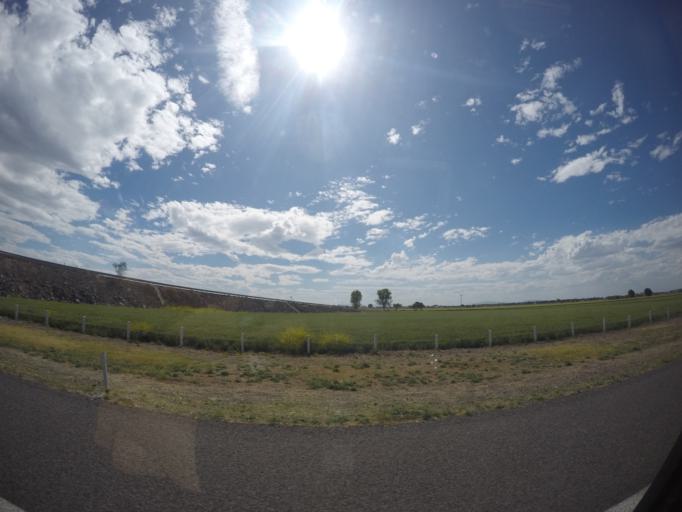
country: MX
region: Guanajuato
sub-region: Salamanca
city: El Recuerdo de Ancon (Xoconoxtle de Arriba)
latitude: 20.6184
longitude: -101.1474
